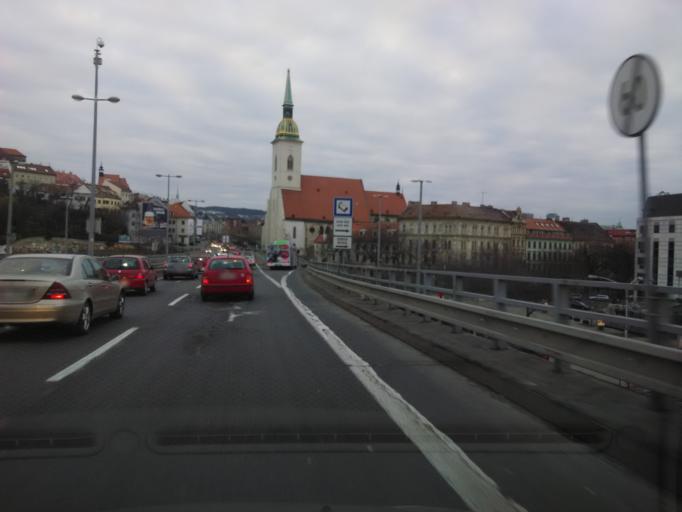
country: SK
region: Bratislavsky
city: Bratislava
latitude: 48.1394
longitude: 17.1046
